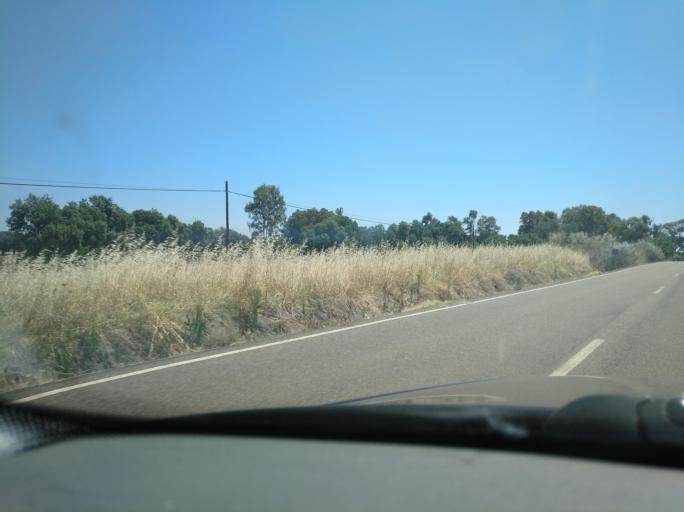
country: ES
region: Extremadura
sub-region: Provincia de Badajoz
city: Olivenza
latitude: 38.7148
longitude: -7.1941
